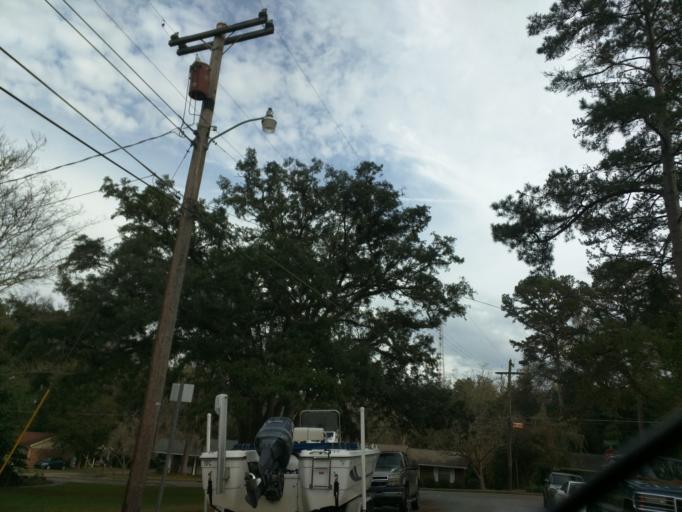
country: US
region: Florida
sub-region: Leon County
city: Tallahassee
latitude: 30.4549
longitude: -84.2501
